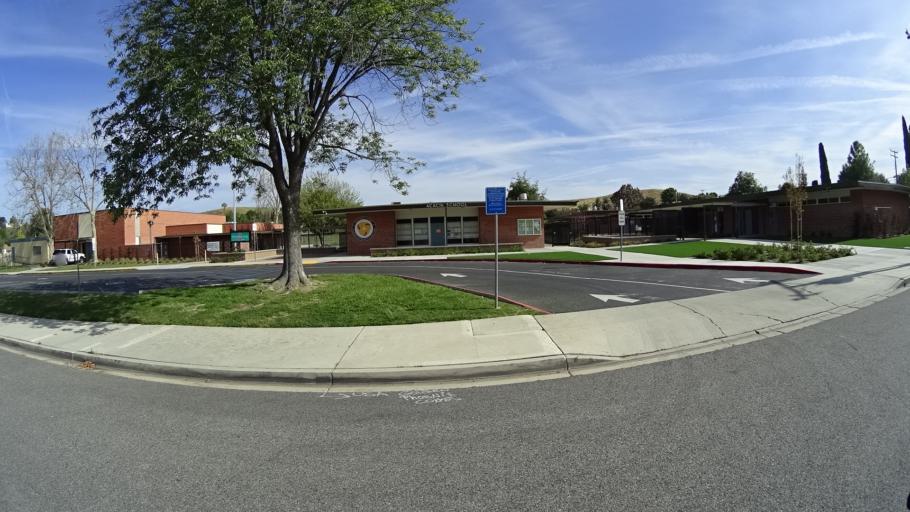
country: US
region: California
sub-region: Ventura County
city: Thousand Oaks
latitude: 34.1967
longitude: -118.8764
